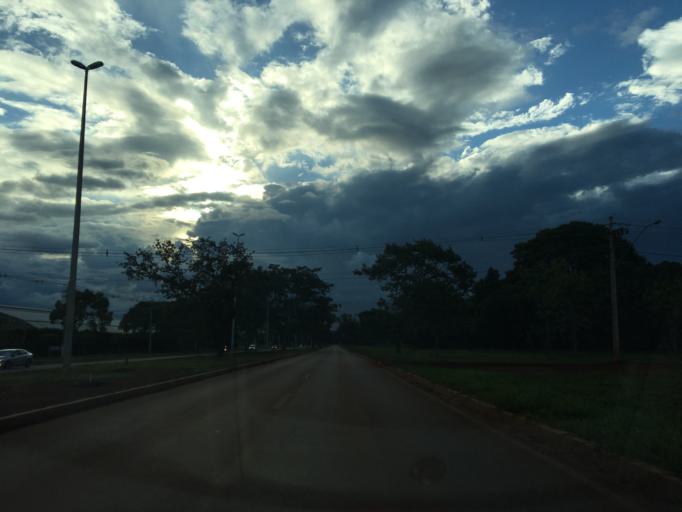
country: BR
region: Federal District
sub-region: Brasilia
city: Brasilia
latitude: -15.8161
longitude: -47.8615
